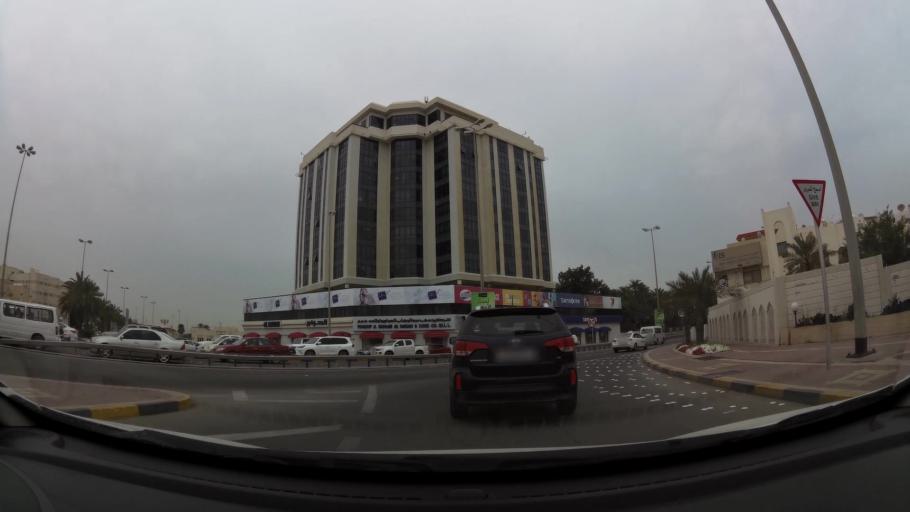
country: BH
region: Manama
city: Manama
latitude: 26.2187
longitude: 50.5664
